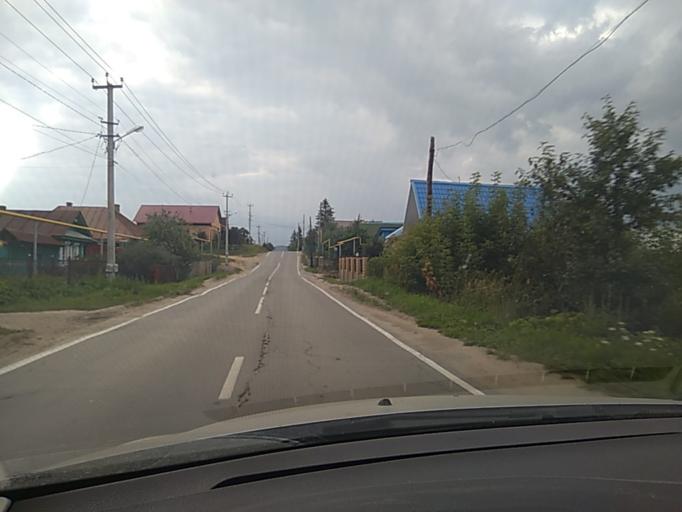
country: RU
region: Chelyabinsk
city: Kyshtym
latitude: 55.6987
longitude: 60.5373
